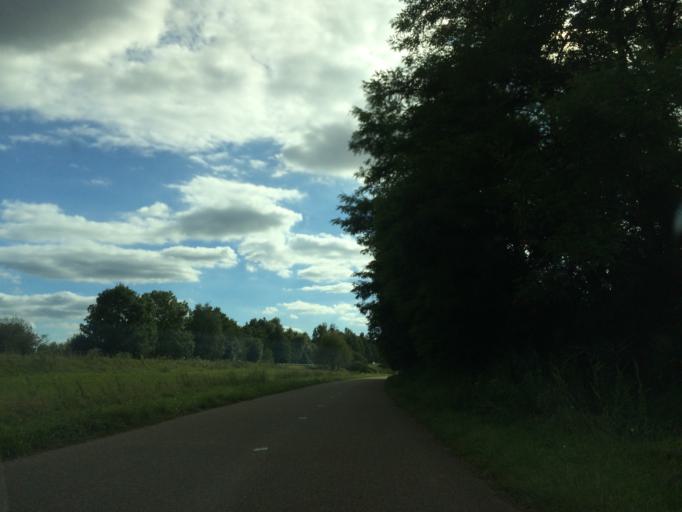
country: FR
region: Alsace
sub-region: Departement du Bas-Rhin
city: Betschdorf
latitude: 48.9357
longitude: 7.9448
